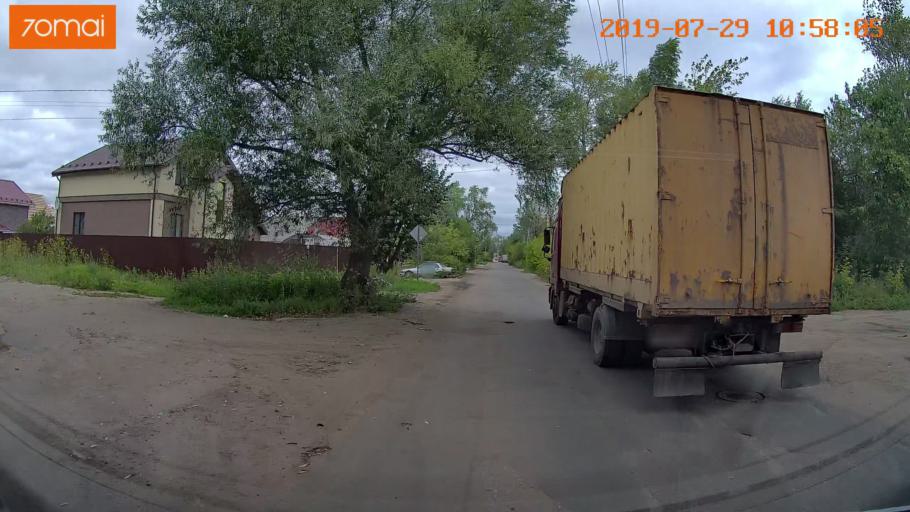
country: RU
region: Ivanovo
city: Bogorodskoye
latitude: 56.9921
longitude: 41.0377
